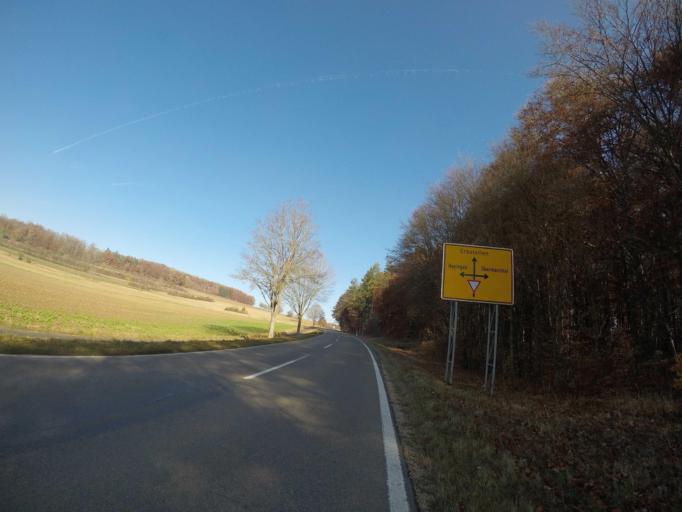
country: DE
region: Baden-Wuerttemberg
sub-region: Tuebingen Region
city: Rechtenstein
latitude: 48.2506
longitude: 9.5315
